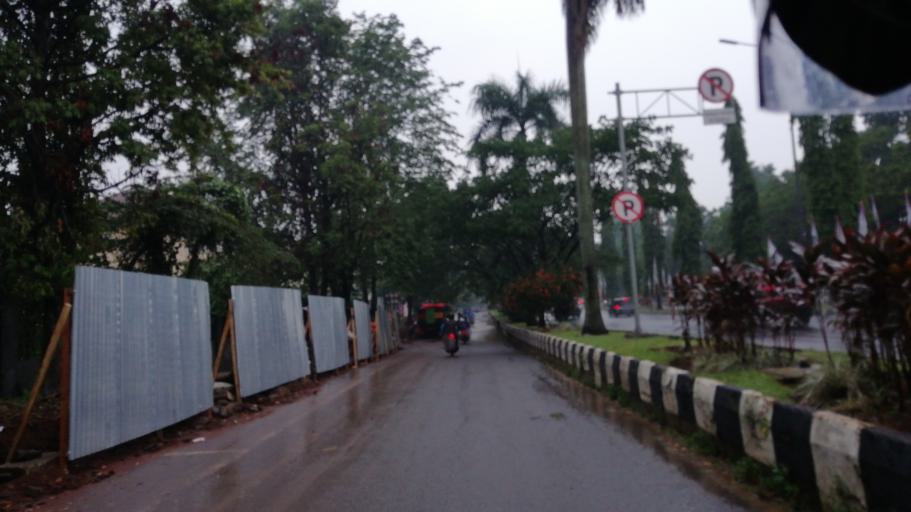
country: ID
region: West Java
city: Cibinong
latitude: -6.4816
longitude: 106.8296
